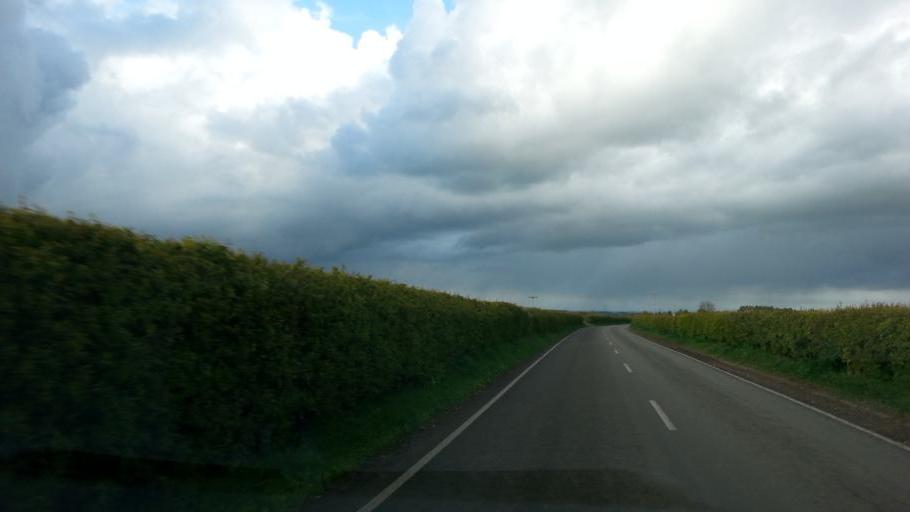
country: GB
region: England
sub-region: Nottinghamshire
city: Southwell
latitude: 53.1158
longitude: -0.9034
